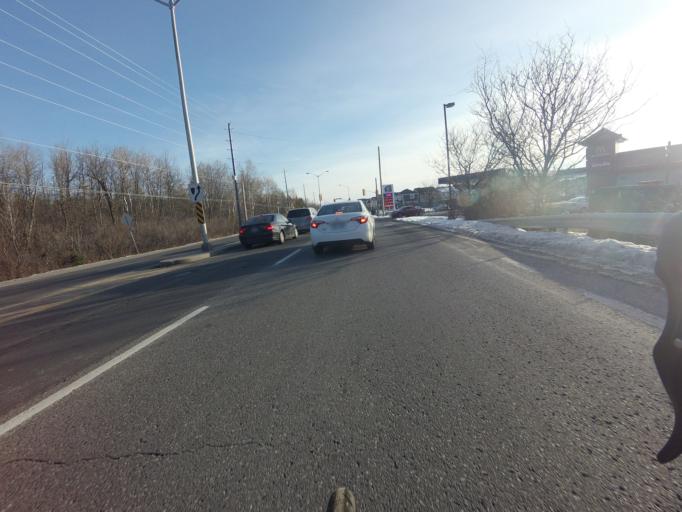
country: CA
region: Ontario
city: Bells Corners
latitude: 45.2817
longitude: -75.8379
